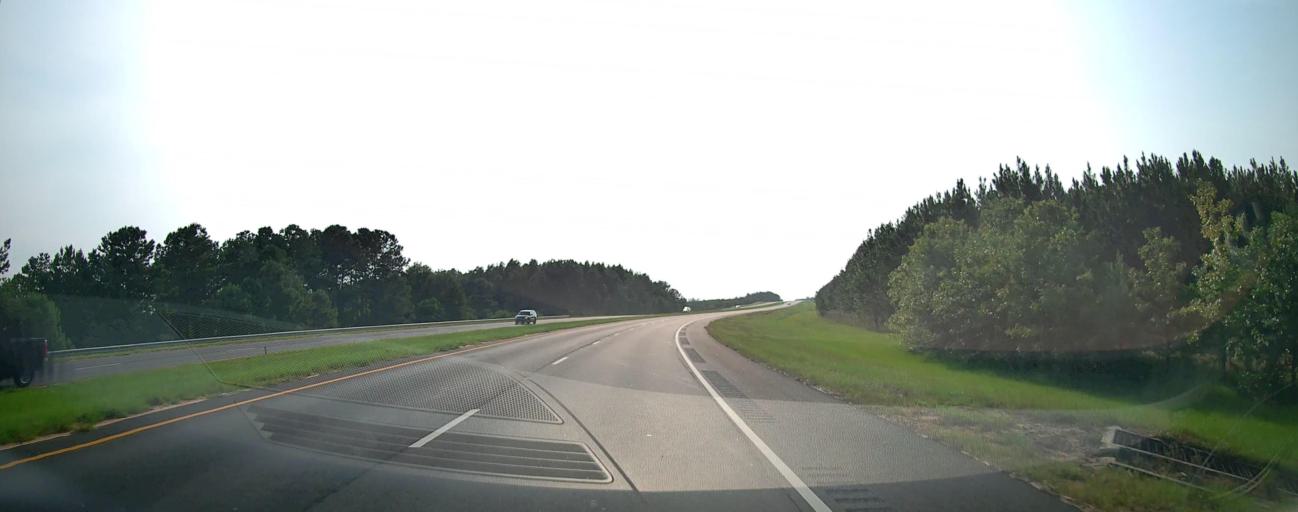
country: US
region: Georgia
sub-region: Taylor County
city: Butler
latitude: 32.5872
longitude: -84.3648
